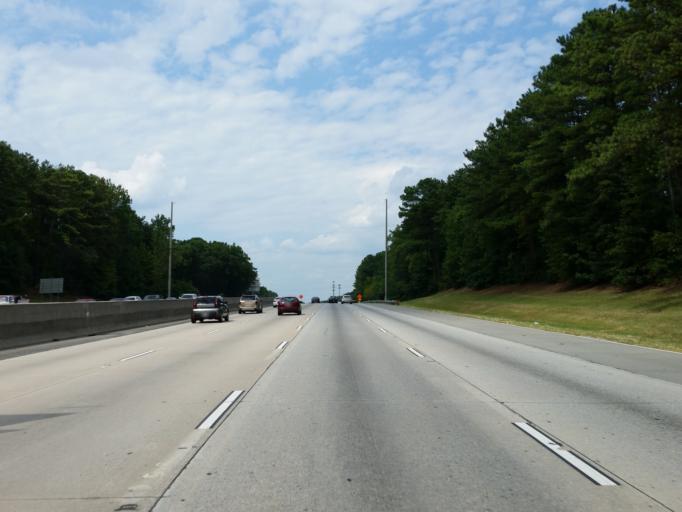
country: US
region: Georgia
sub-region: DeKalb County
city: Dunwoody
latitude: 33.9599
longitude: -84.3542
